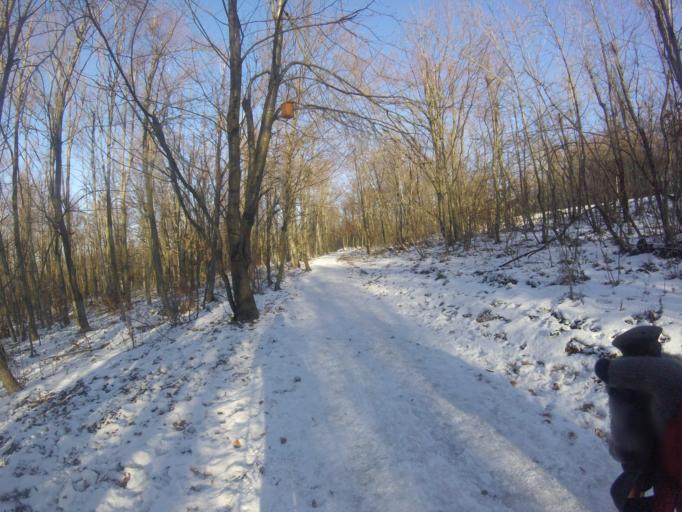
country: HU
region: Pest
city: Budakeszi
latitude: 47.5088
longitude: 18.9564
